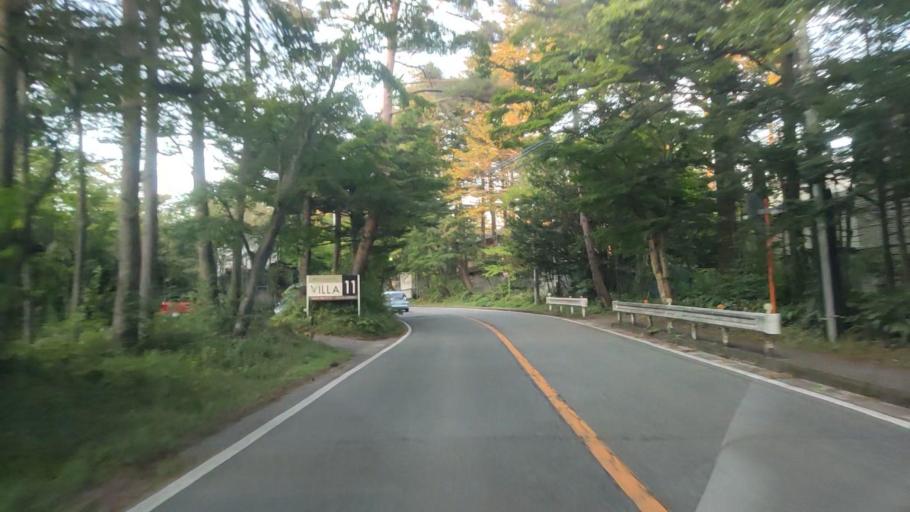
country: JP
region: Nagano
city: Komoro
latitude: 36.3678
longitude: 138.5873
